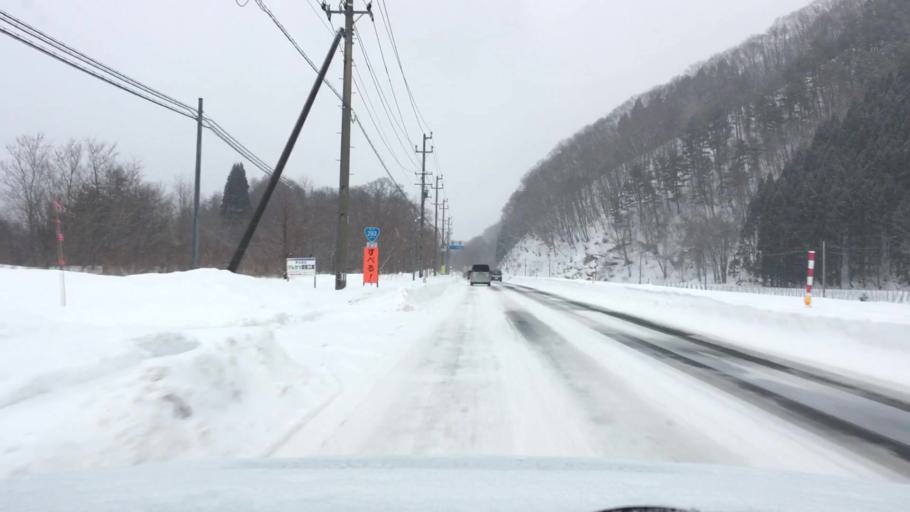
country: JP
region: Akita
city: Hanawa
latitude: 40.0395
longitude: 140.9953
